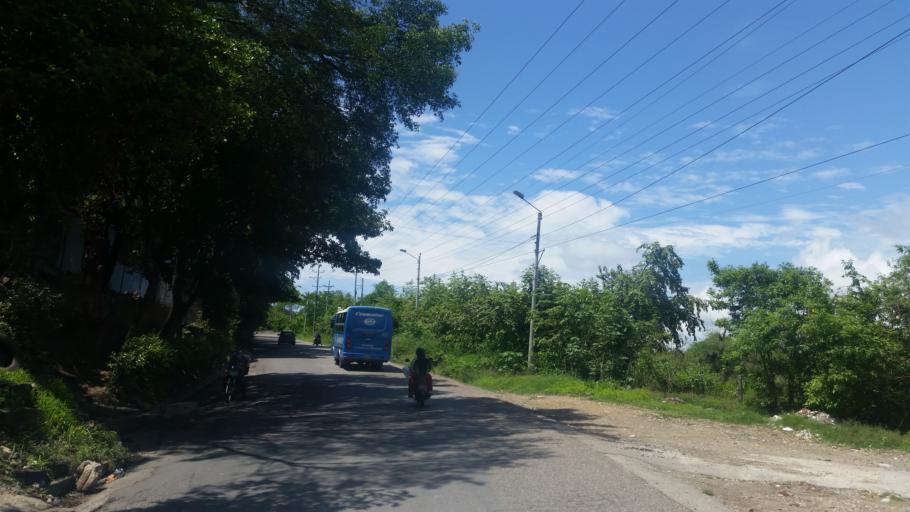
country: CO
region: Huila
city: Neiva
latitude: 2.9825
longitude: -75.2825
